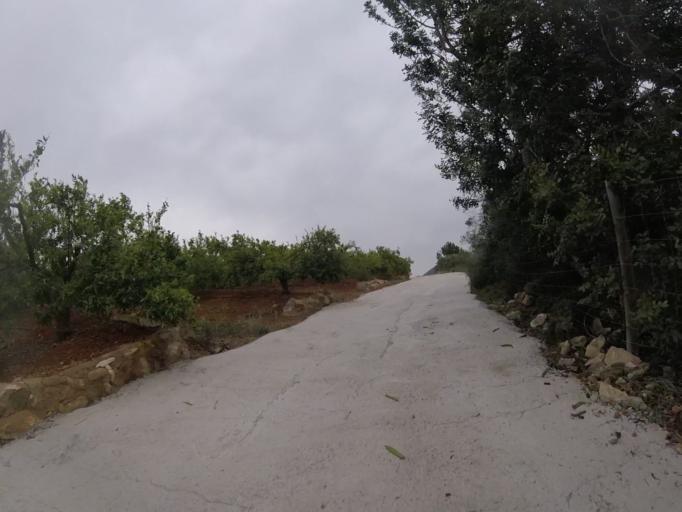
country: ES
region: Valencia
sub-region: Provincia de Castello
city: Alcala de Xivert
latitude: 40.2777
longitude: 0.2535
